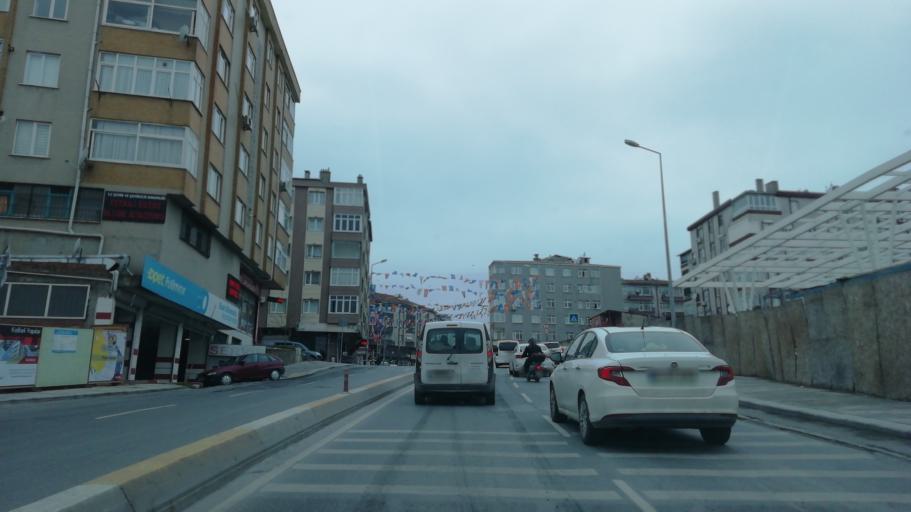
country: TR
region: Istanbul
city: Mahmutbey
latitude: 41.0097
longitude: 28.8003
